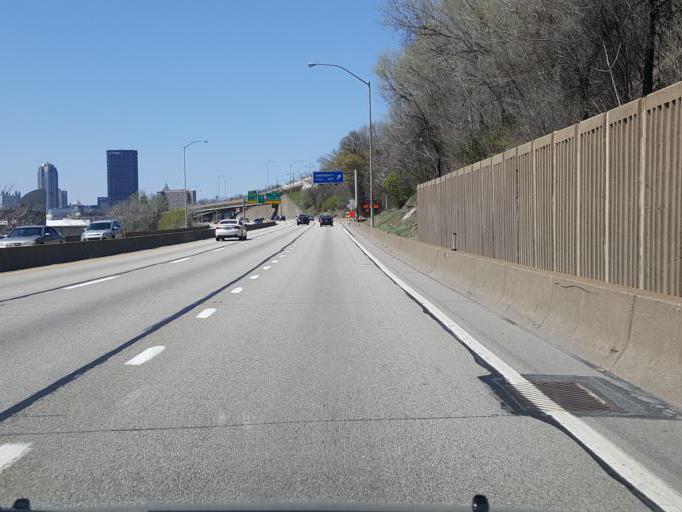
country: US
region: Pennsylvania
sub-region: Allegheny County
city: Bloomfield
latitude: 40.4343
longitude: -79.9646
